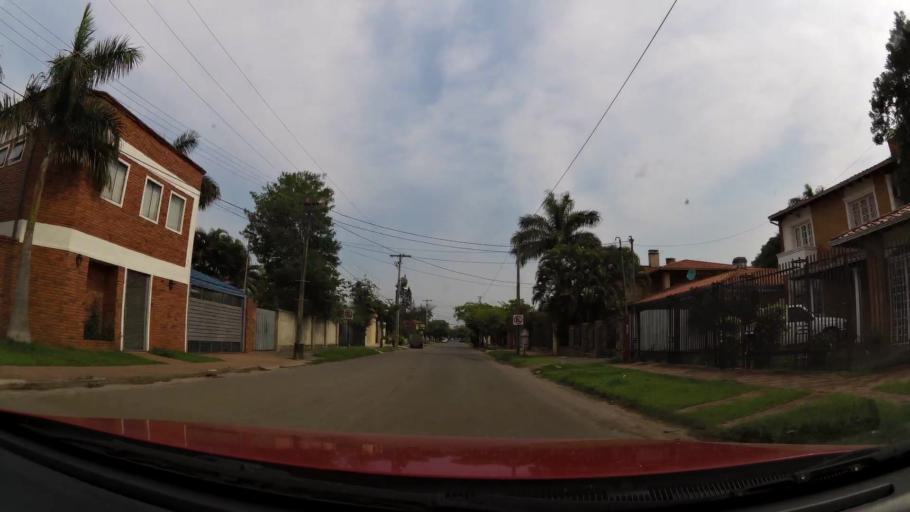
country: PY
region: Central
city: Fernando de la Mora
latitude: -25.2776
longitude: -57.5493
